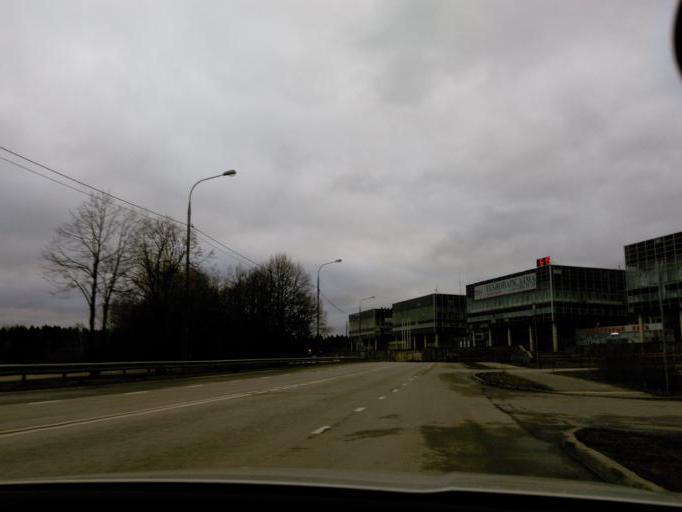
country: RU
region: Moskovskaya
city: Rzhavki
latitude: 55.9853
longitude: 37.2174
